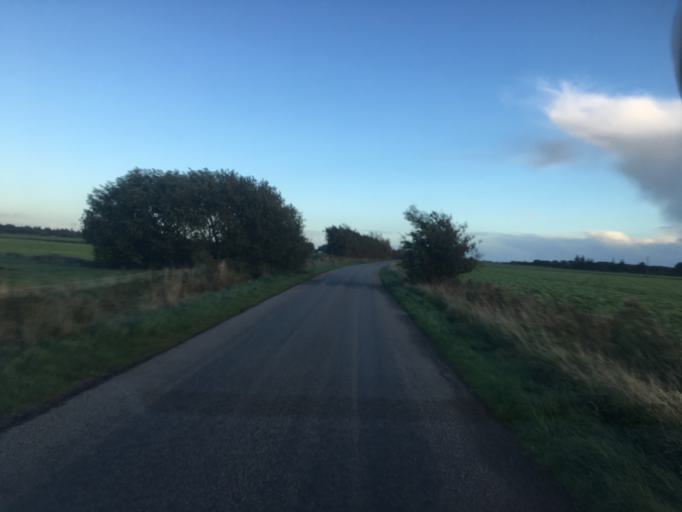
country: DE
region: Schleswig-Holstein
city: Ellhoft
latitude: 54.9583
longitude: 9.0154
